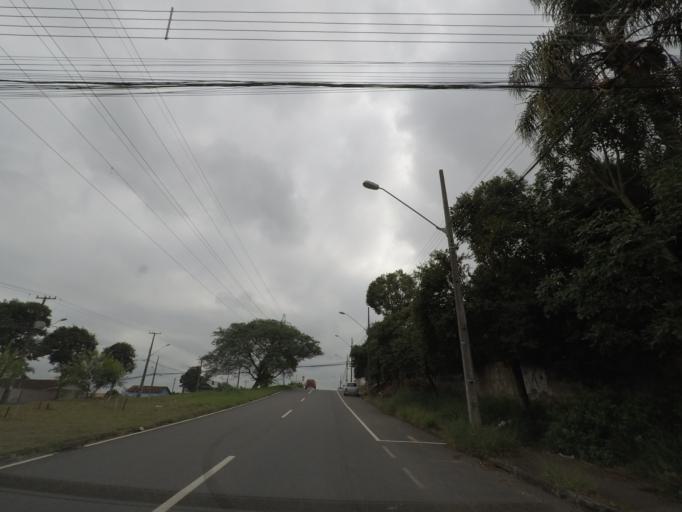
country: BR
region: Parana
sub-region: Curitiba
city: Curitiba
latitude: -25.5005
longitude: -49.3164
